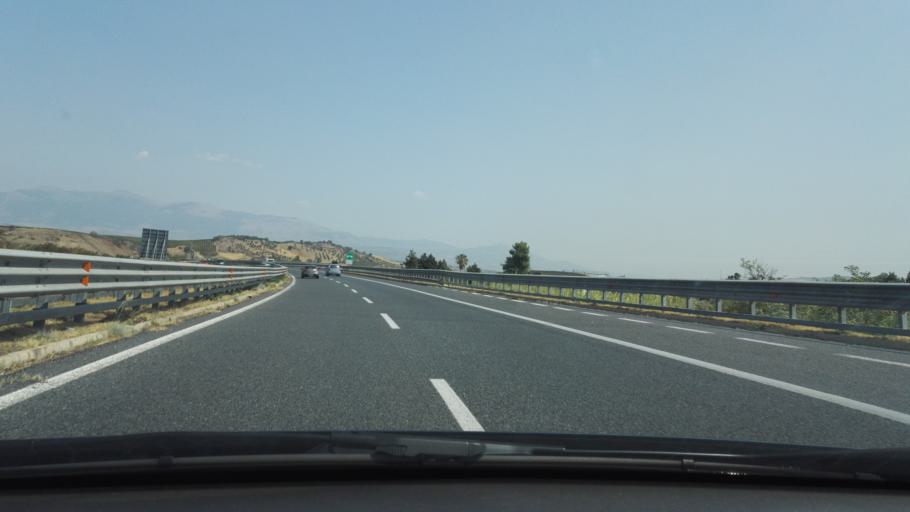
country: IT
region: Calabria
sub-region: Provincia di Cosenza
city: Tarsia
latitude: 39.6327
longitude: 16.2316
